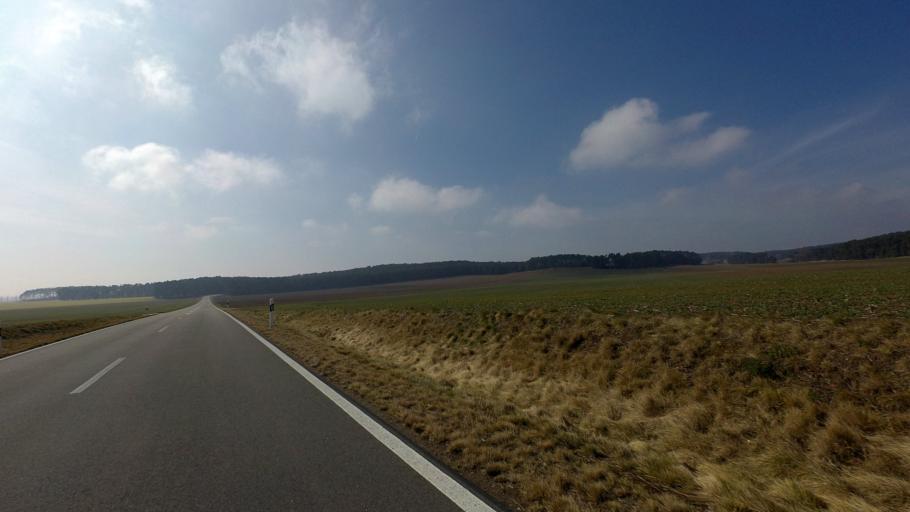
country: DE
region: Brandenburg
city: Belzig
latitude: 52.1190
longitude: 12.6289
